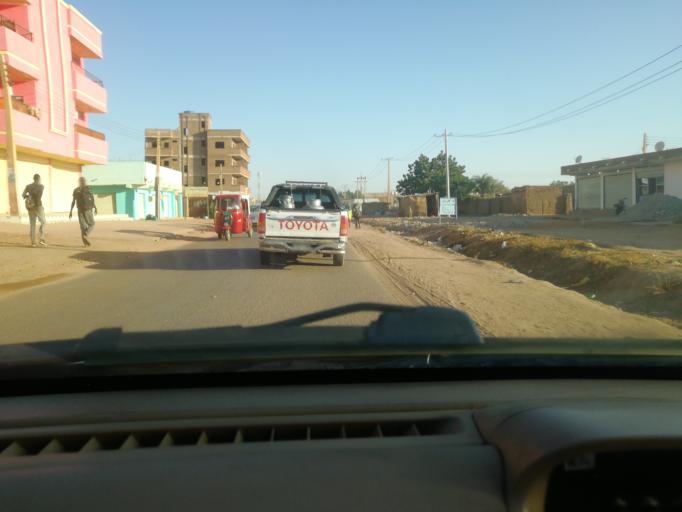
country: SD
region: Khartoum
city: Khartoum
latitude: 15.5949
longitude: 32.6368
